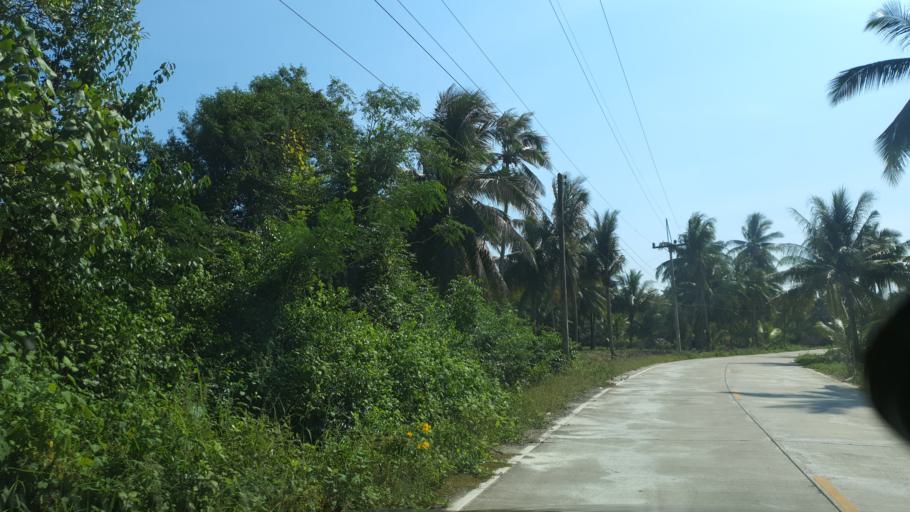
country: TH
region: Surat Thani
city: Tha Chana
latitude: 9.5960
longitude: 99.2053
